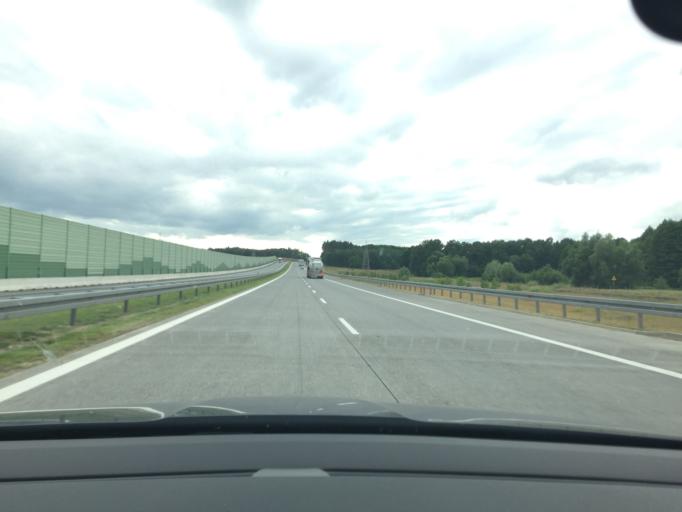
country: PL
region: Lubusz
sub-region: Powiat miedzyrzecki
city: Brojce
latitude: 52.2979
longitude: 15.6754
